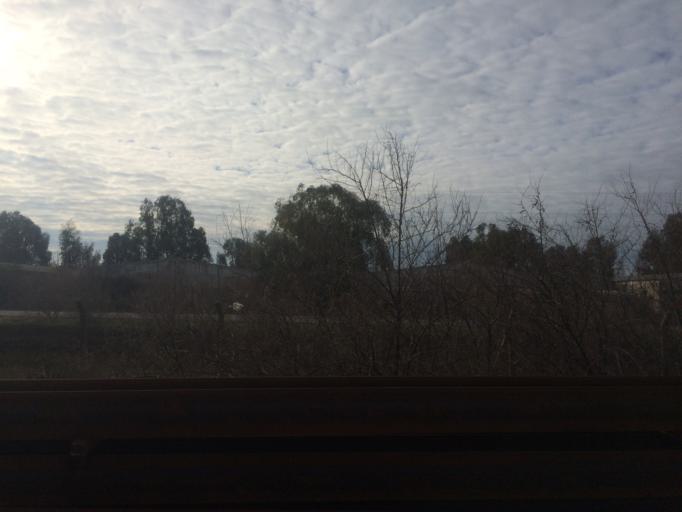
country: TR
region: Izmir
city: Karsiyaka
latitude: 38.4920
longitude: 26.9442
